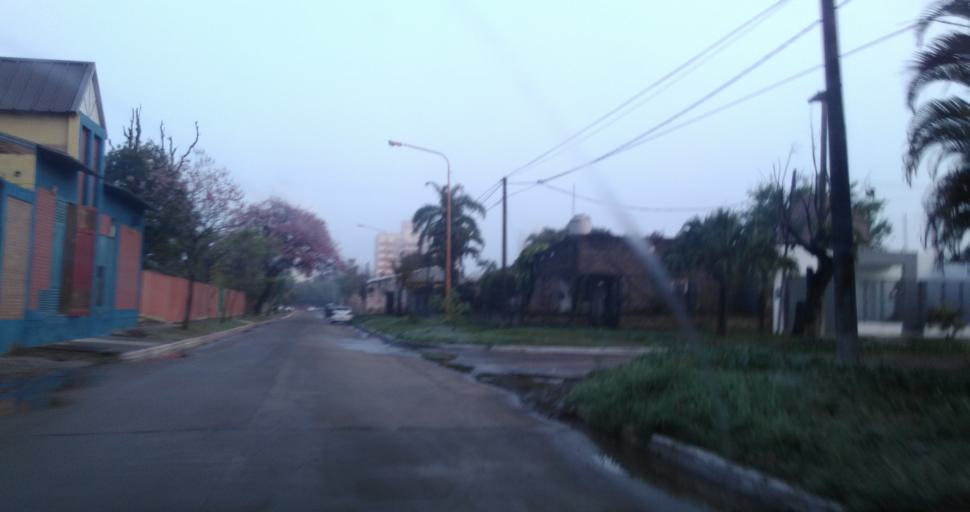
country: AR
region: Chaco
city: Resistencia
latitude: -27.4566
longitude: -58.9745
